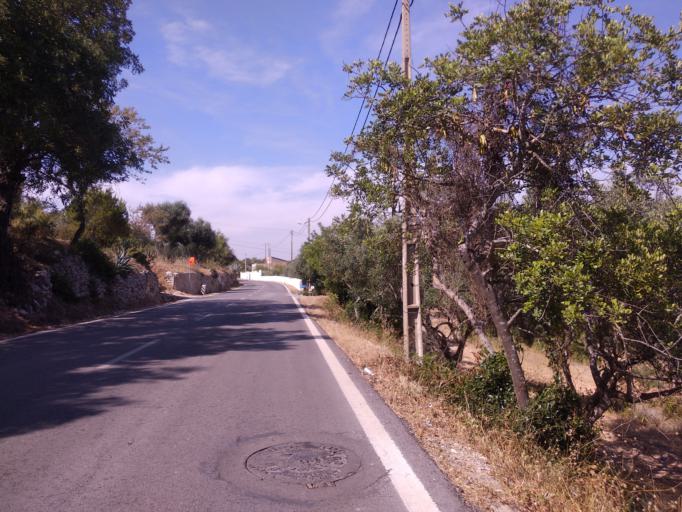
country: PT
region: Faro
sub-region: Faro
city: Santa Barbara de Nexe
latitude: 37.1147
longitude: -7.9598
